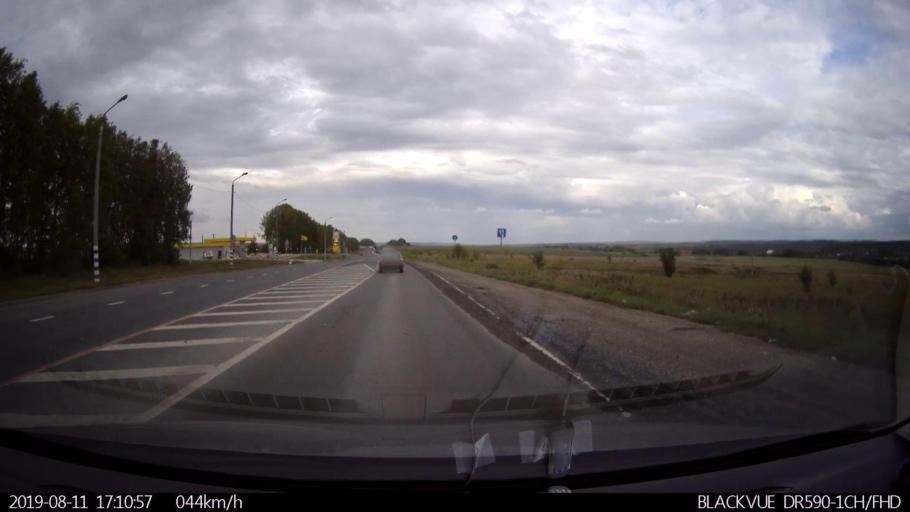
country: RU
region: Ulyanovsk
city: Mayna
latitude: 54.2996
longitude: 47.8797
